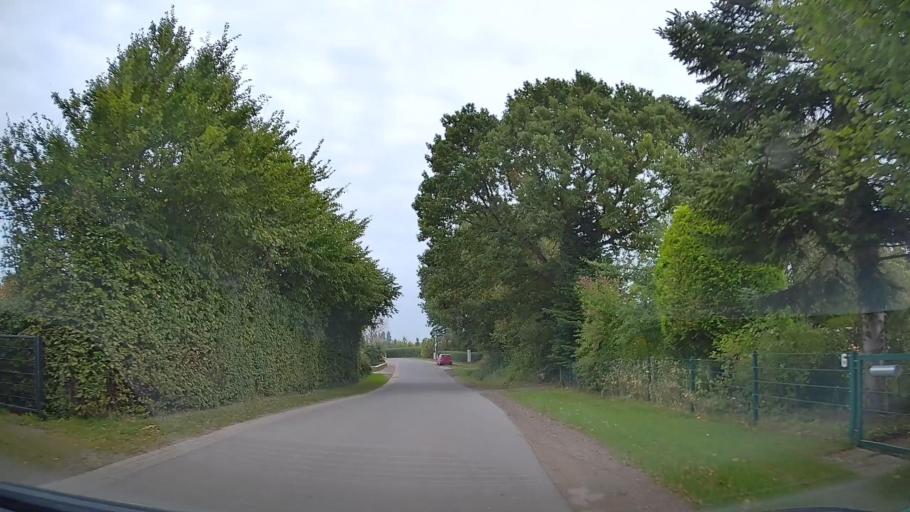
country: DE
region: Schleswig-Holstein
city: Hohenfelde
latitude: 54.3705
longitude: 10.5139
